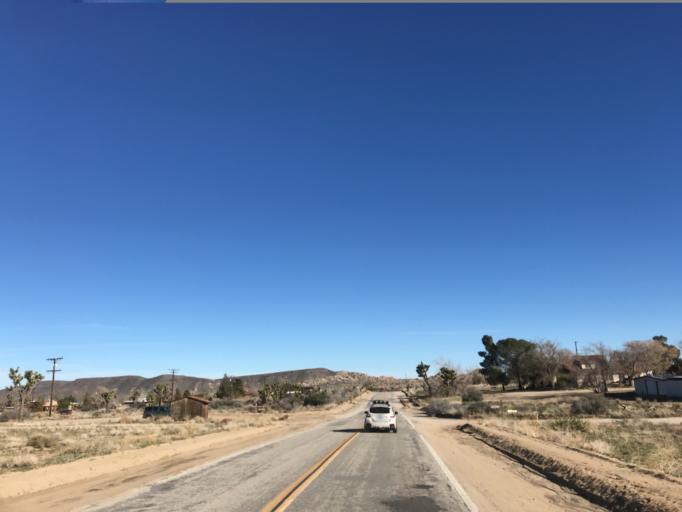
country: US
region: California
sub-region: San Bernardino County
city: Yucca Valley
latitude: 34.1562
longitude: -116.5000
